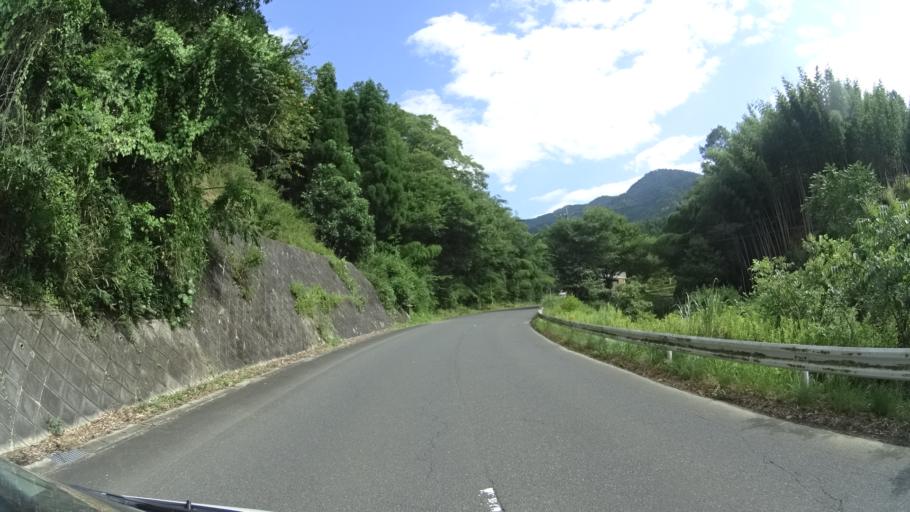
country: JP
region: Kyoto
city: Fukuchiyama
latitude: 35.3631
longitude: 135.1348
